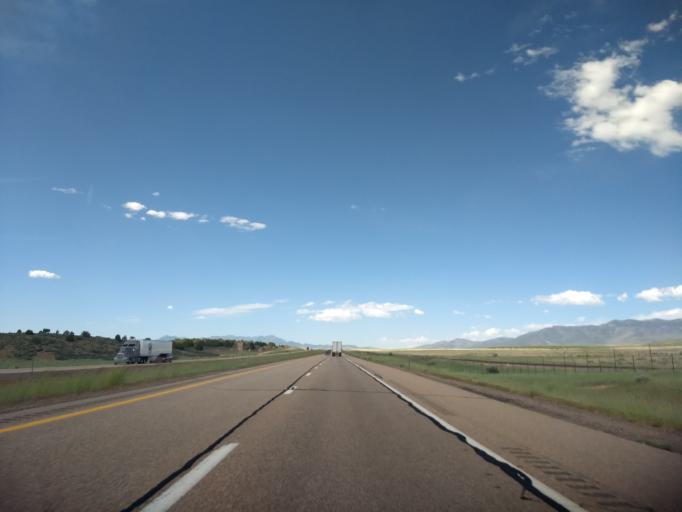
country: US
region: Utah
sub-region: Millard County
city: Fillmore
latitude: 39.0097
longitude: -112.3098
